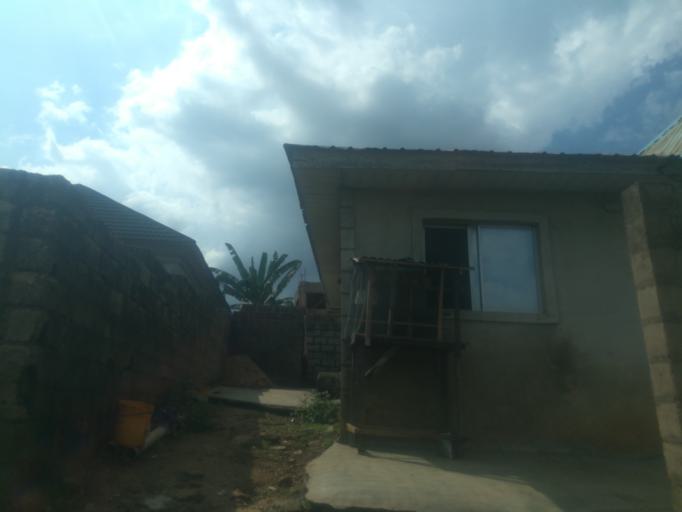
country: NG
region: Oyo
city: Ibadan
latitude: 7.4209
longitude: 3.8375
